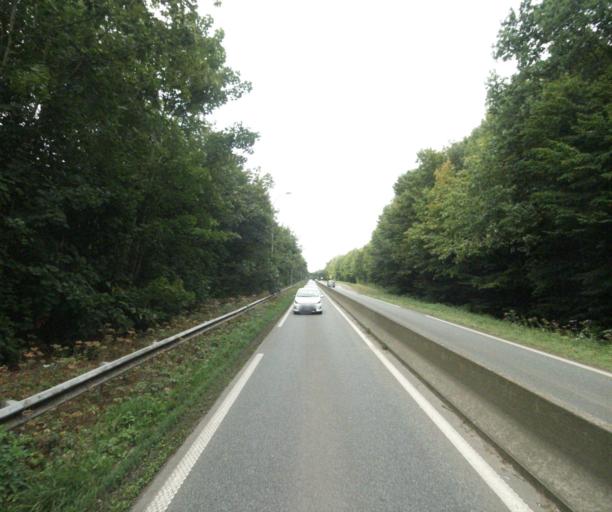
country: FR
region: Nord-Pas-de-Calais
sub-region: Departement du Nord
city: Lys-lez-Lannoy
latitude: 50.6705
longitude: 3.2231
